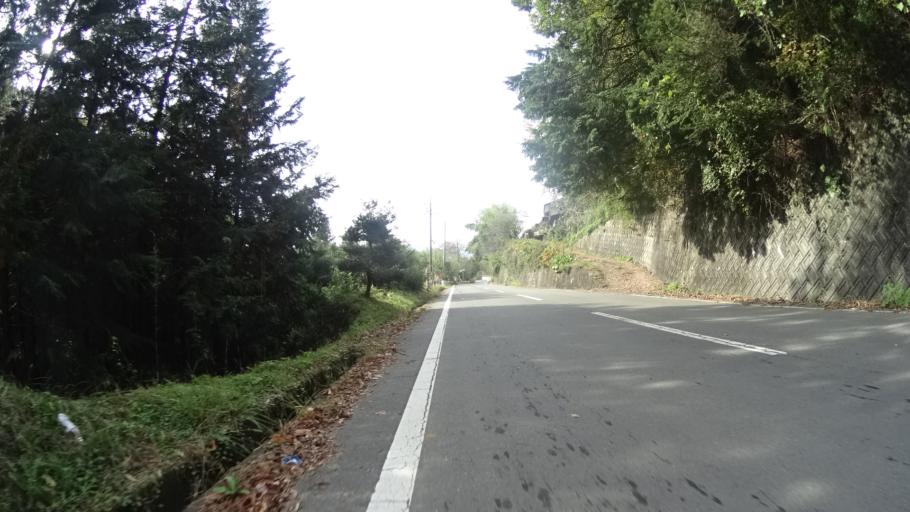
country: JP
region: Yamanashi
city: Otsuki
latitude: 35.6240
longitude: 139.0207
